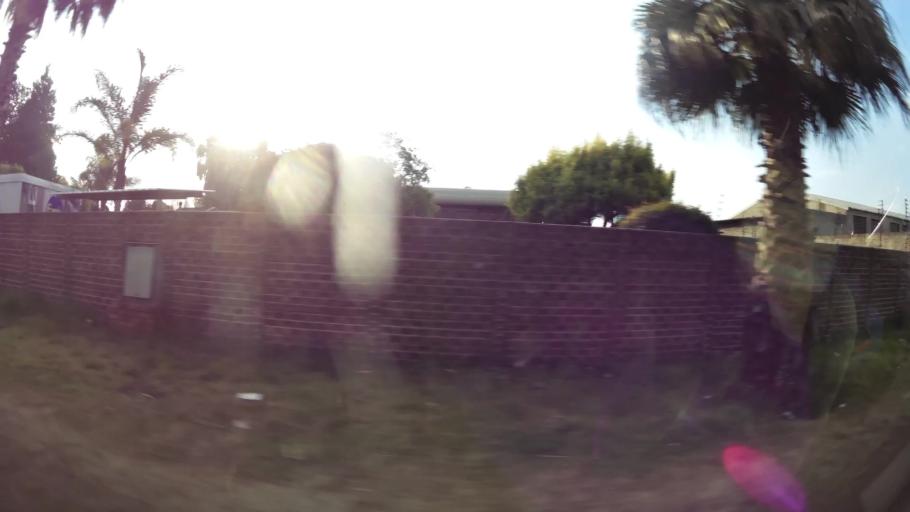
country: ZA
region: Gauteng
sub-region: Ekurhuleni Metropolitan Municipality
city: Benoni
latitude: -26.1216
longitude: 28.2927
